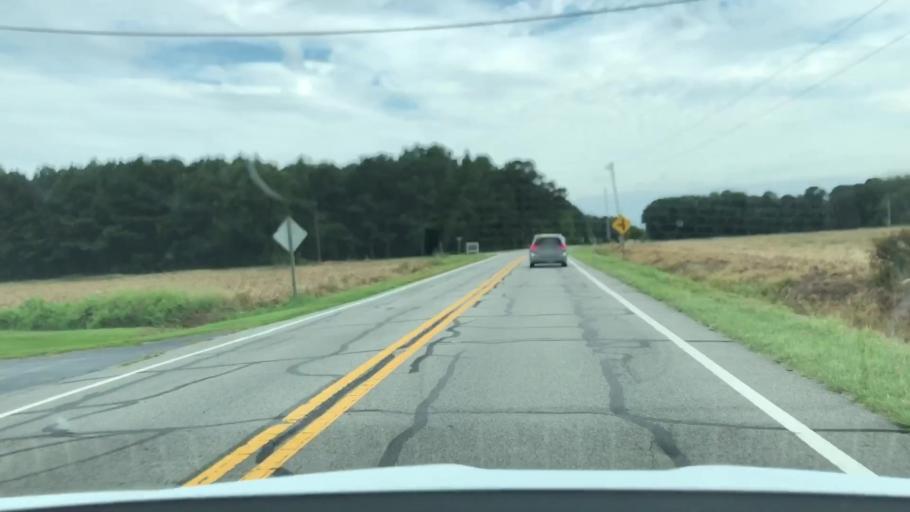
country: US
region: North Carolina
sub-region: Lenoir County
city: Kinston
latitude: 35.1615
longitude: -77.5556
